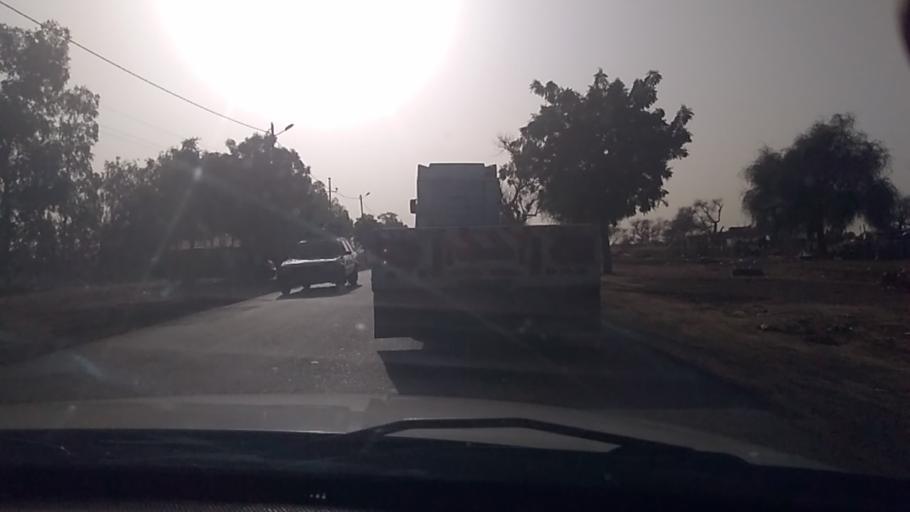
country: SN
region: Thies
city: Khombole
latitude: 14.7664
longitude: -16.7395
